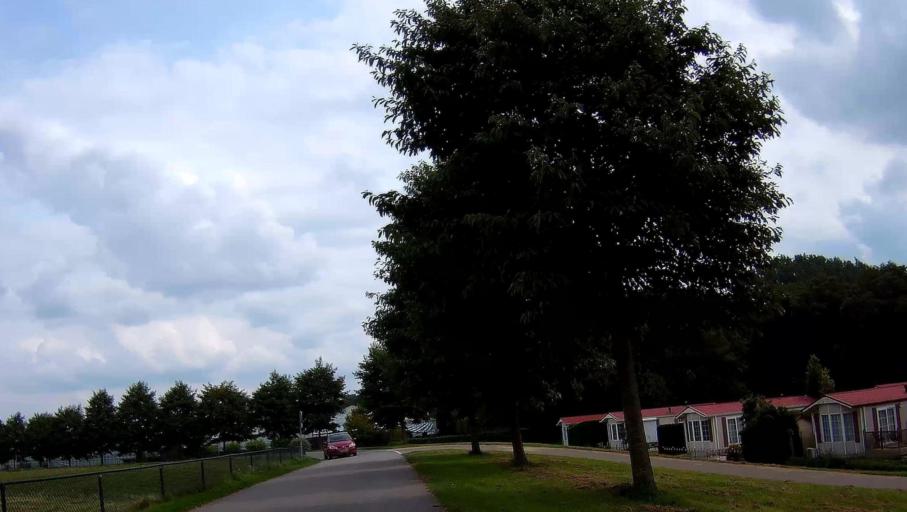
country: NL
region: South Holland
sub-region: Gemeente Westland
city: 's-Gravenzande
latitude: 51.9774
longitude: 4.1765
